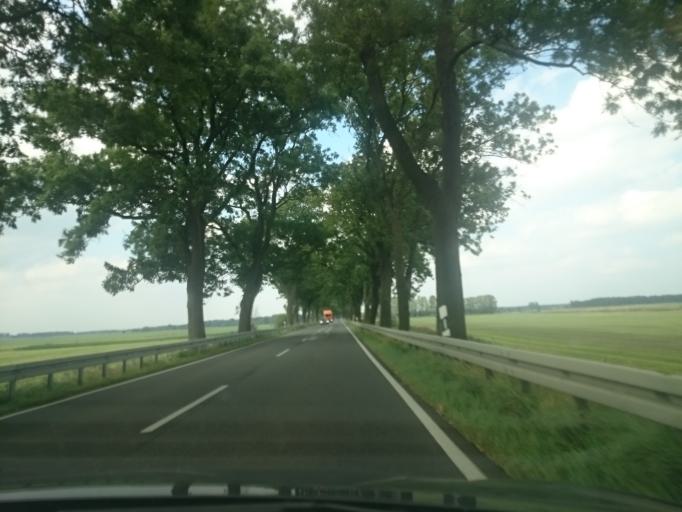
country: DE
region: Mecklenburg-Vorpommern
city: Ferdinandshof
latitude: 53.6767
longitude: 13.8851
